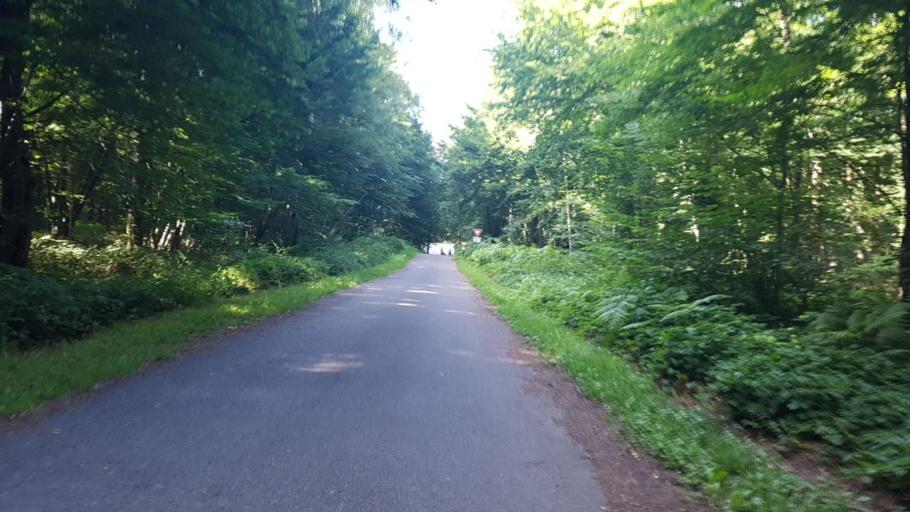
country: FR
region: Picardie
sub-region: Departement de l'Oise
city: Ver-sur-Launette
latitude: 49.1160
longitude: 2.6558
